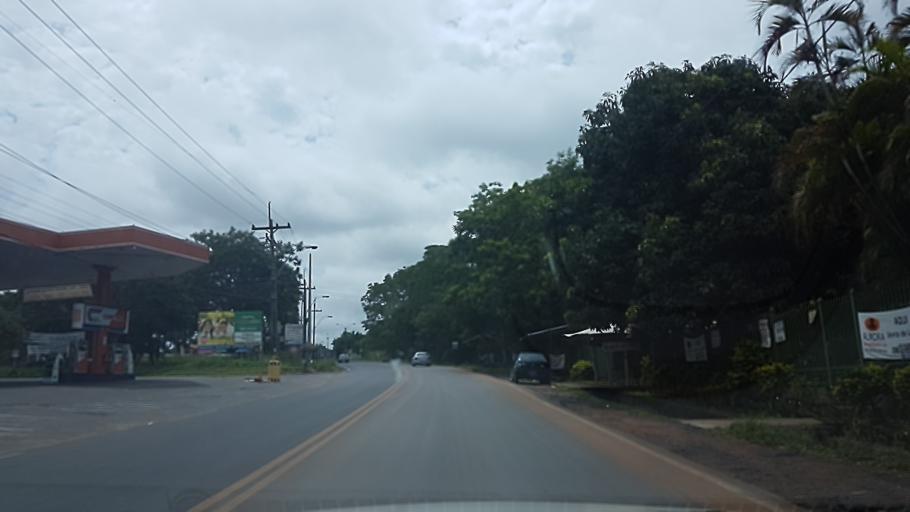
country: PY
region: Central
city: San Antonio
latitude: -25.4044
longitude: -57.5721
